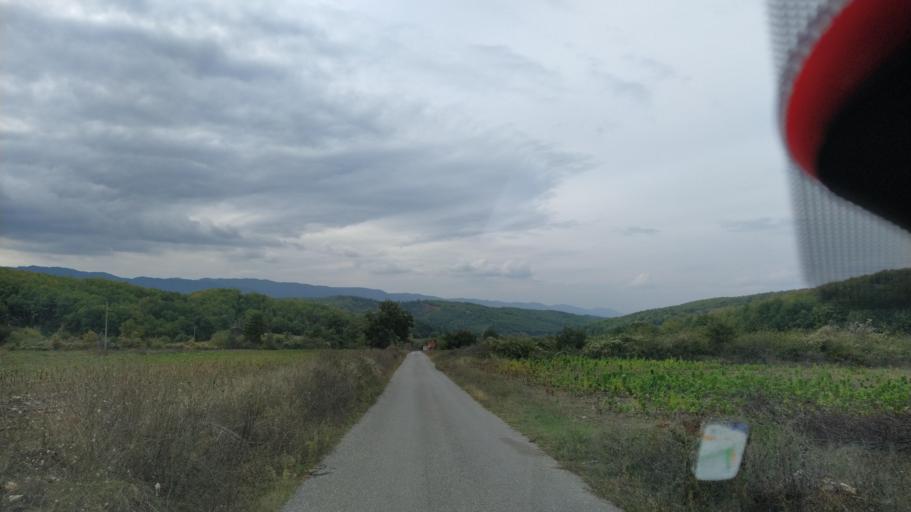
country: MK
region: Konce
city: Konce
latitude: 41.5069
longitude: 22.4678
